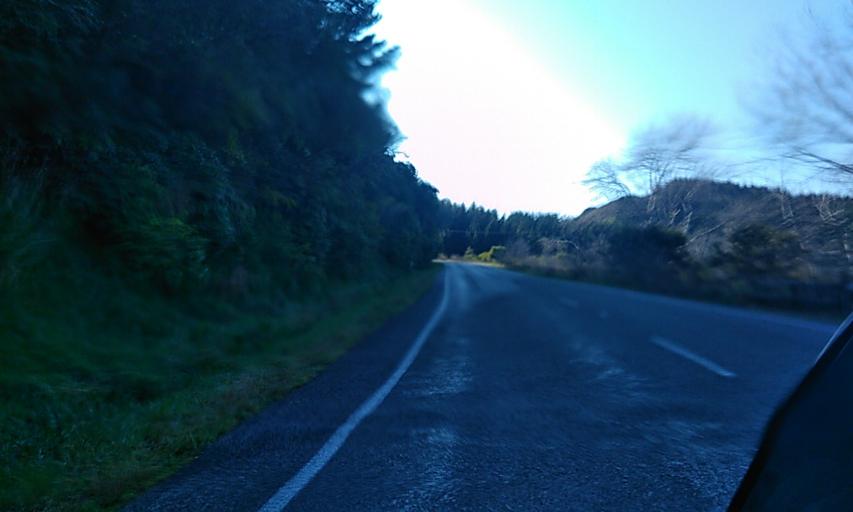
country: NZ
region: Gisborne
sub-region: Gisborne District
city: Gisborne
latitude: -38.5941
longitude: 177.9761
